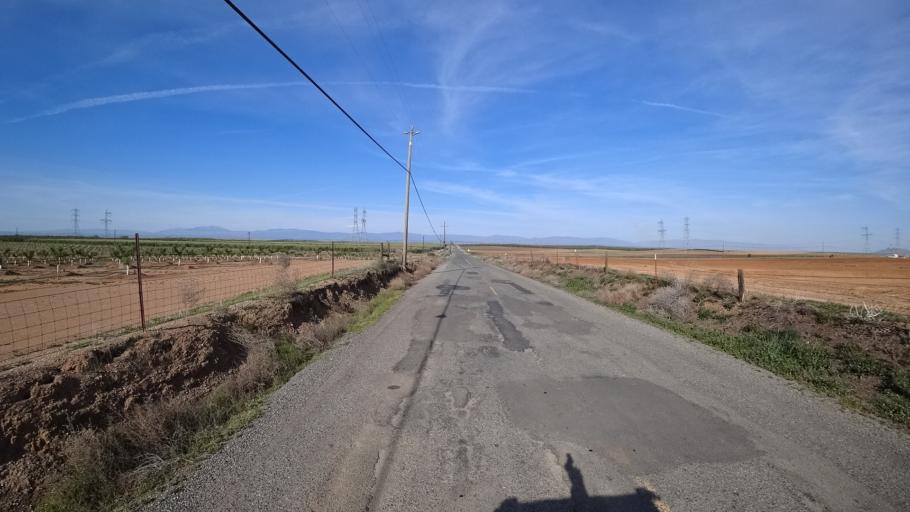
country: US
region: California
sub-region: Glenn County
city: Orland
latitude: 39.6684
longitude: -122.2697
